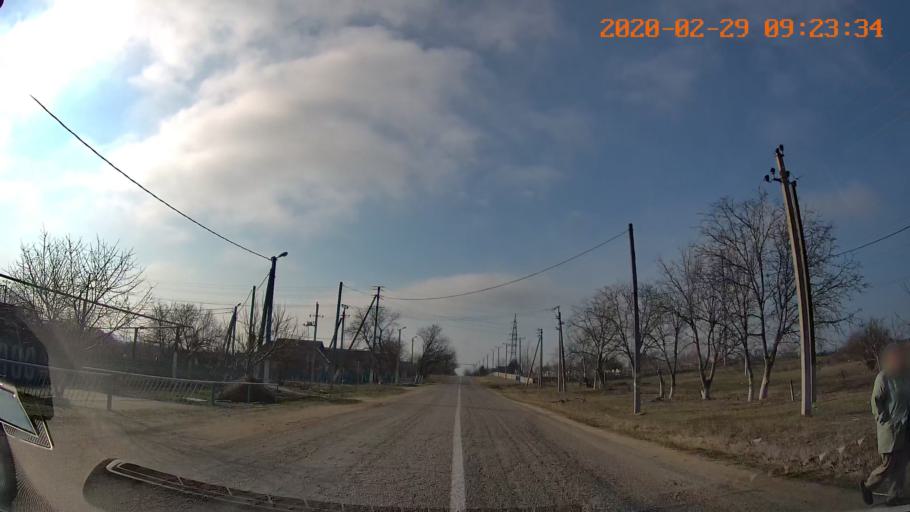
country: MD
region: Telenesti
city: Pervomaisc
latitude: 46.7245
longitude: 29.9609
